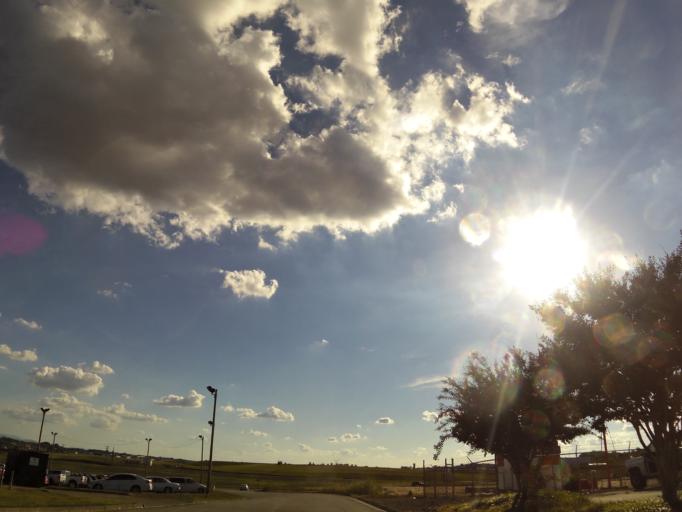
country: US
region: Tennessee
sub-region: Blount County
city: Alcoa
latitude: 35.8267
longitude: -83.9779
